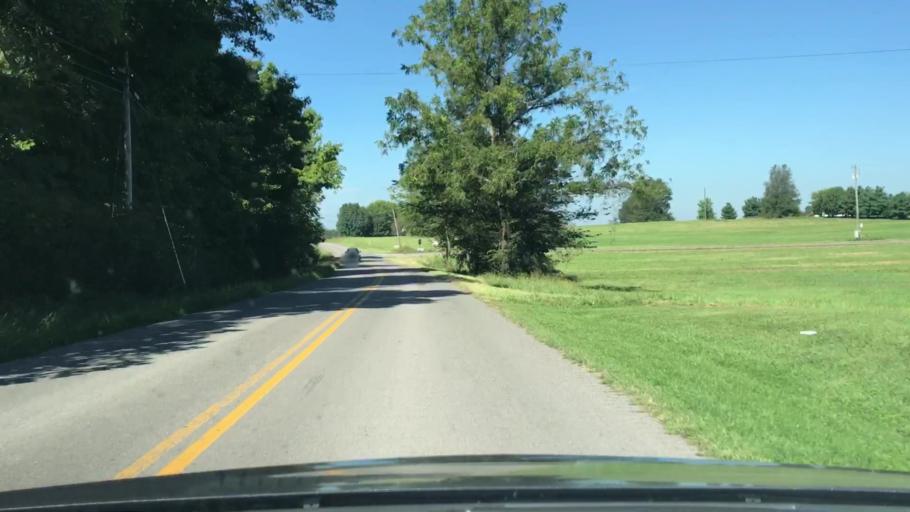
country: US
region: Kentucky
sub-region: Hardin County
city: Elizabethtown
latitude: 37.6018
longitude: -85.8860
